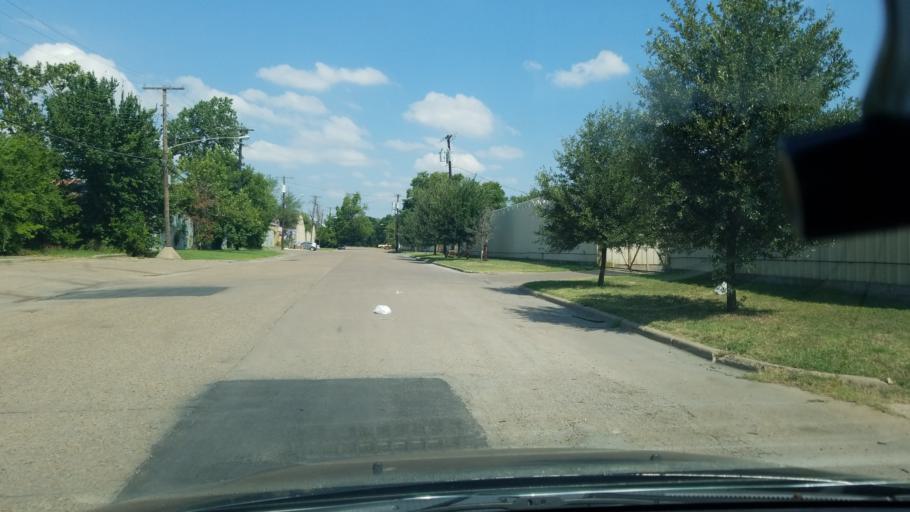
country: US
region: Texas
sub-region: Dallas County
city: Dallas
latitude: 32.7590
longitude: -96.7952
